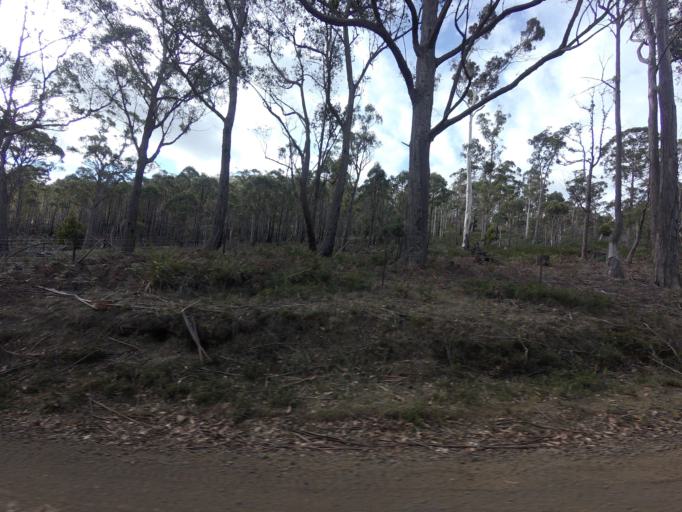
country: AU
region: Tasmania
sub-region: Brighton
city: Bridgewater
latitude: -42.4893
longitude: 147.3116
